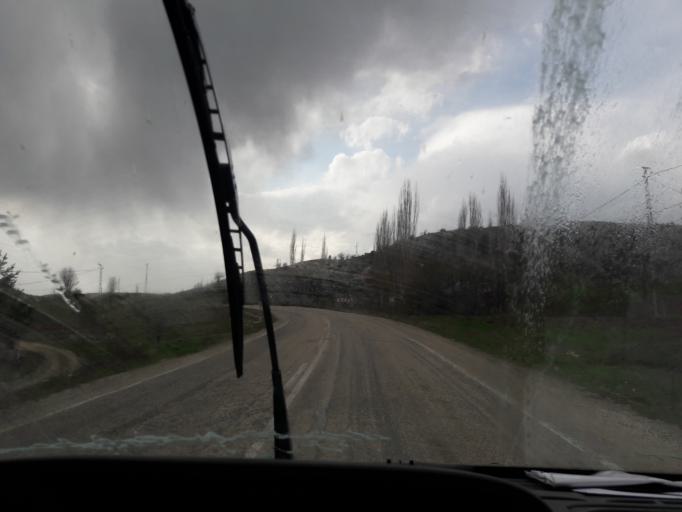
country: TR
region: Giresun
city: Alucra
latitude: 40.2975
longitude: 38.8028
